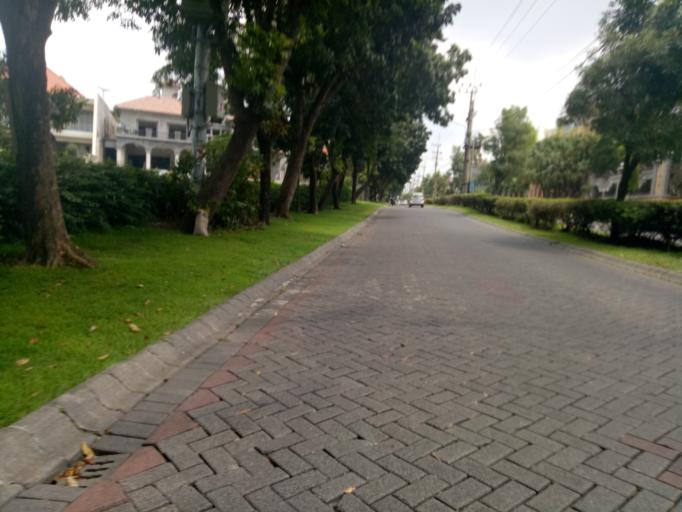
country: ID
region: East Java
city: Jagirsidosermo
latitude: -7.2910
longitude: 112.6857
